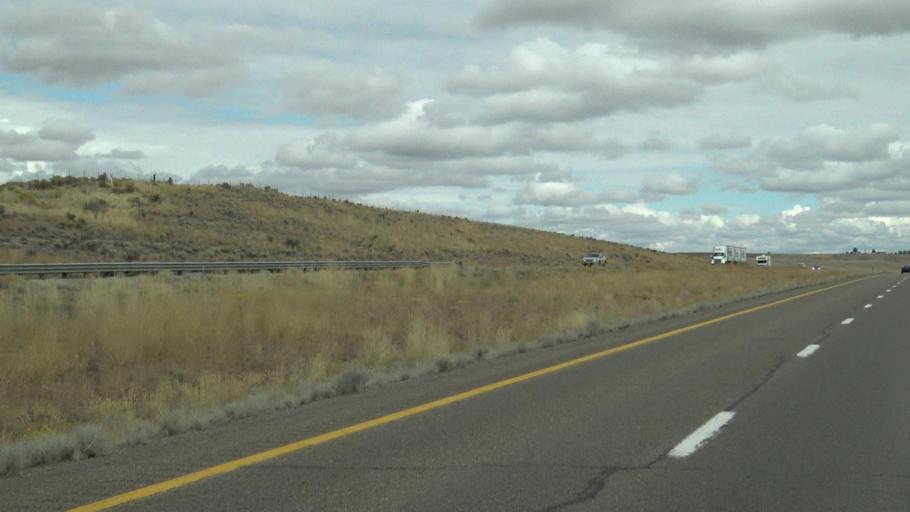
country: US
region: Nevada
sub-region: Elko County
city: Elko
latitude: 40.9082
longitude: -115.6974
